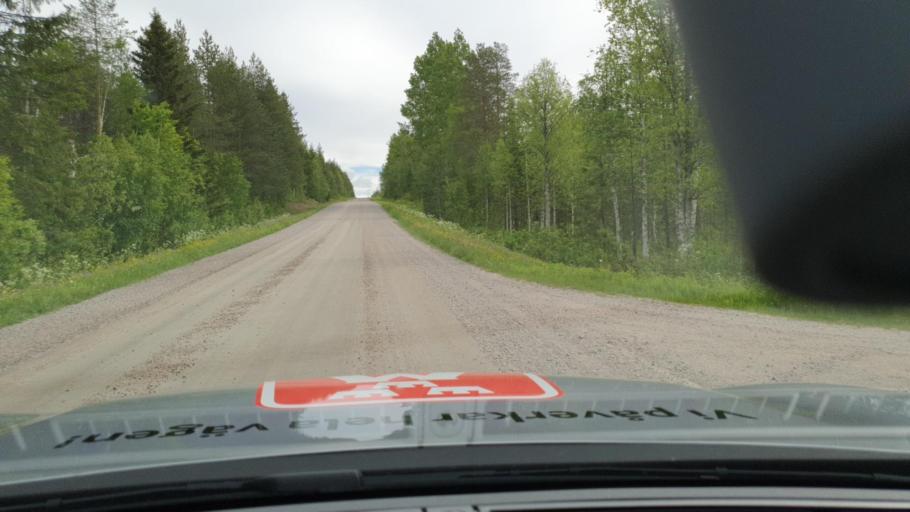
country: SE
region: Norrbotten
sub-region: Kalix Kommun
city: Kalix
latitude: 65.9249
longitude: 23.4908
